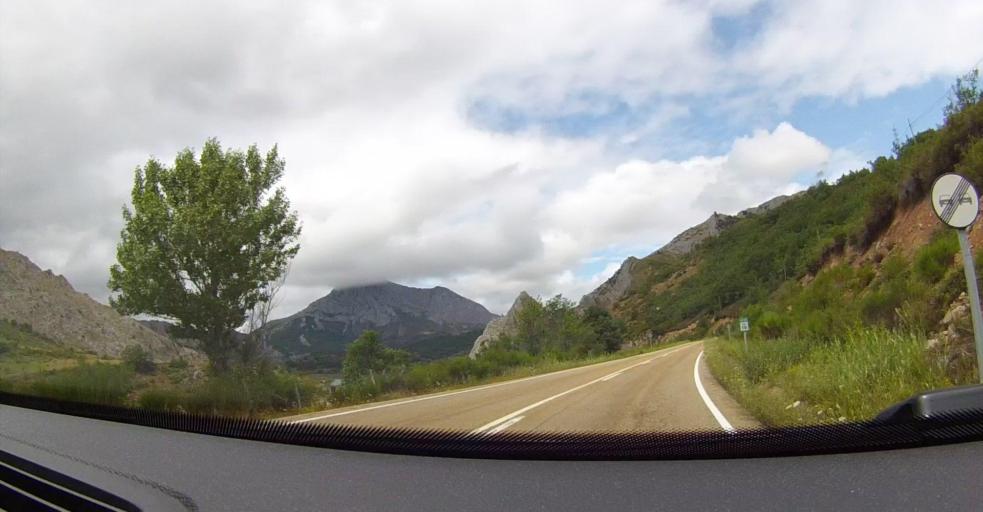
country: ES
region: Castille and Leon
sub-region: Provincia de Leon
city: Reyero
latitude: 42.9548
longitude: -5.2495
